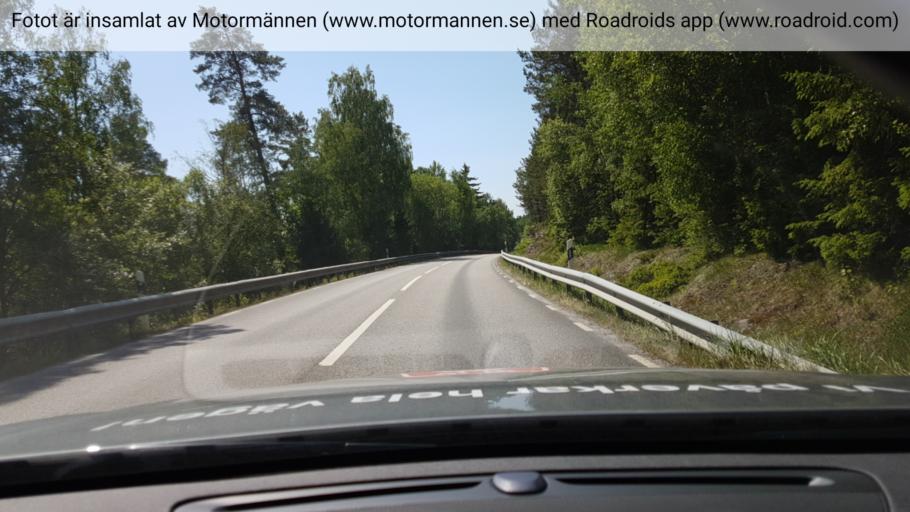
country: SE
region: Stockholm
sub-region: Norrtalje Kommun
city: Rimbo
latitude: 59.6638
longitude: 18.3461
